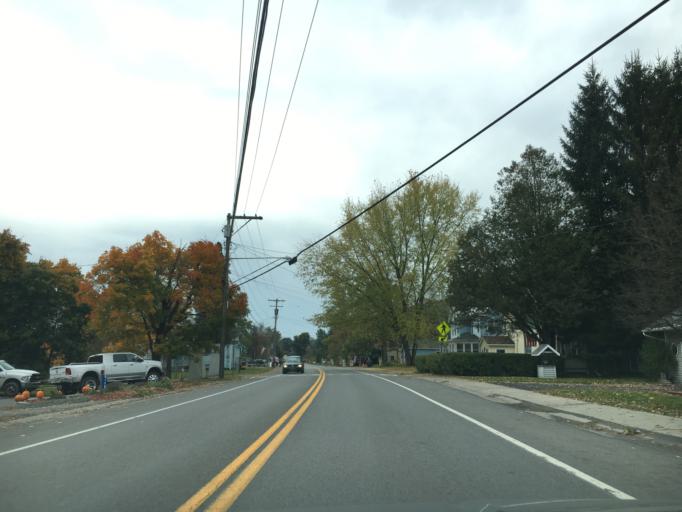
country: US
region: New York
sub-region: Otsego County
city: Cooperstown
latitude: 42.5887
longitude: -74.9466
